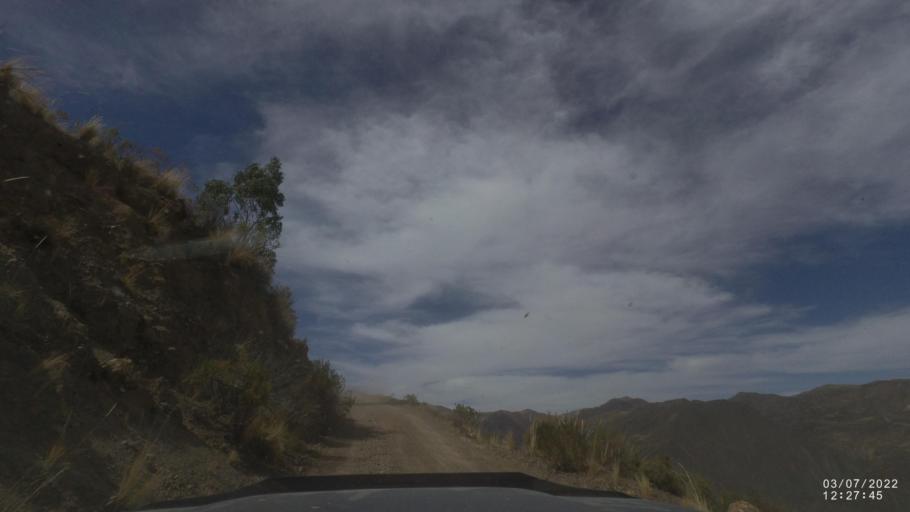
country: BO
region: Cochabamba
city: Irpa Irpa
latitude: -17.8126
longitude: -66.6135
